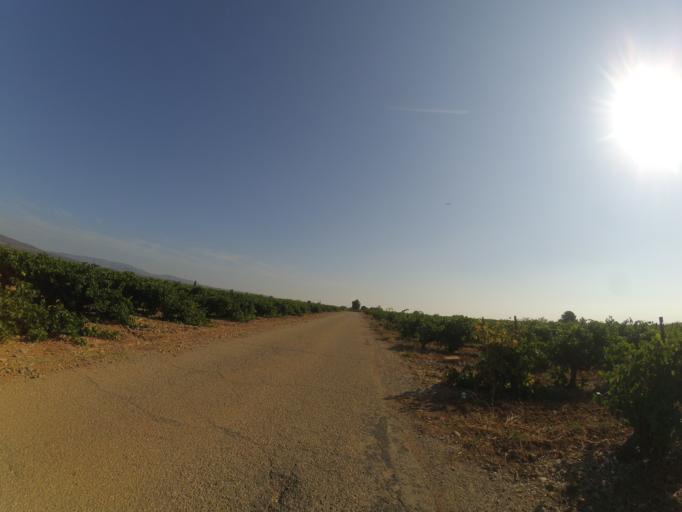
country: FR
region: Languedoc-Roussillon
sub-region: Departement des Pyrenees-Orientales
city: Rivesaltes
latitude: 42.7925
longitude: 2.8483
